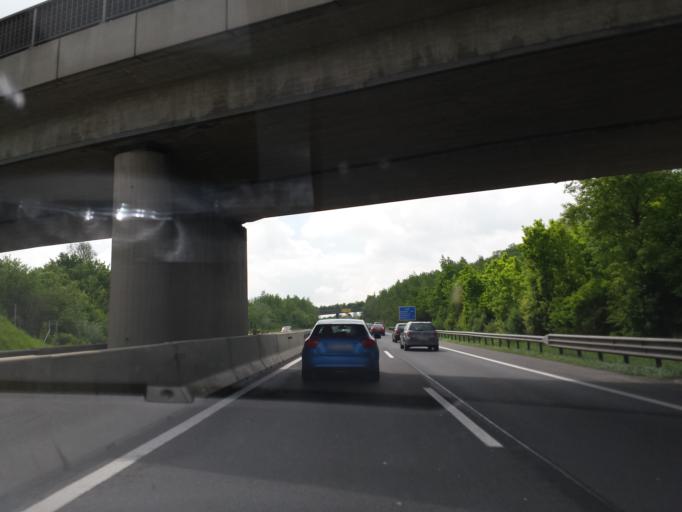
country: AT
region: Burgenland
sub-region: Politischer Bezirk Neusiedl am See
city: Parndorf
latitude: 47.9996
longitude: 16.8331
